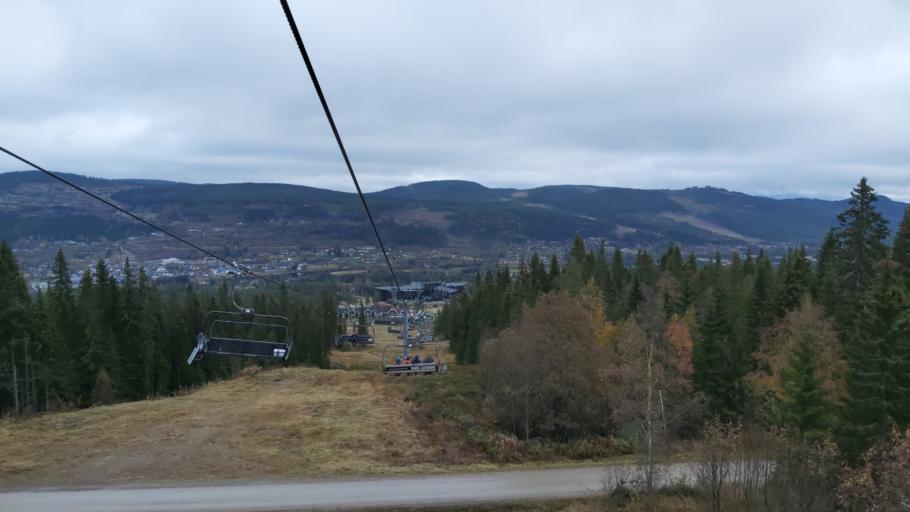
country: NO
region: Hedmark
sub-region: Trysil
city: Innbygda
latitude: 61.3081
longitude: 12.2279
